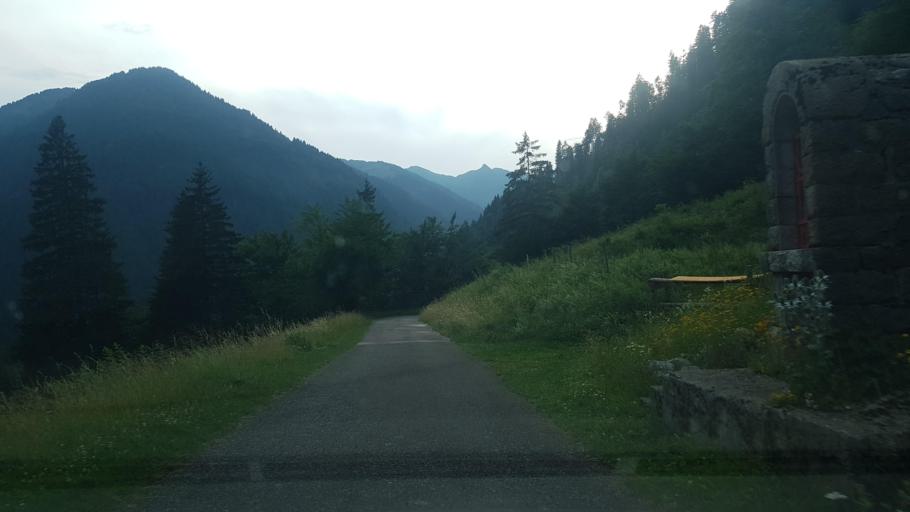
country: IT
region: Friuli Venezia Giulia
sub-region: Provincia di Udine
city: Paularo
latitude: 46.5803
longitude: 13.1202
